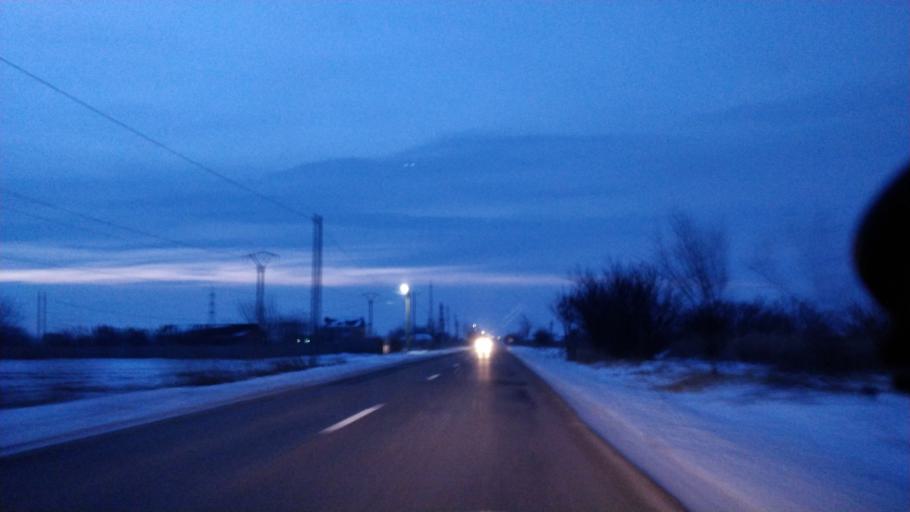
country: RO
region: Vrancea
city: Vulturu de Sus
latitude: 45.6081
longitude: 27.4452
